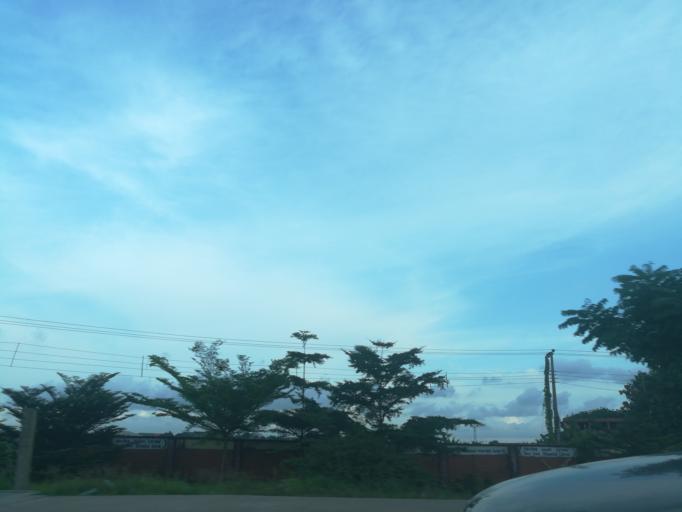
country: NG
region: Lagos
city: Ebute Ikorodu
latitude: 6.6207
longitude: 3.4804
